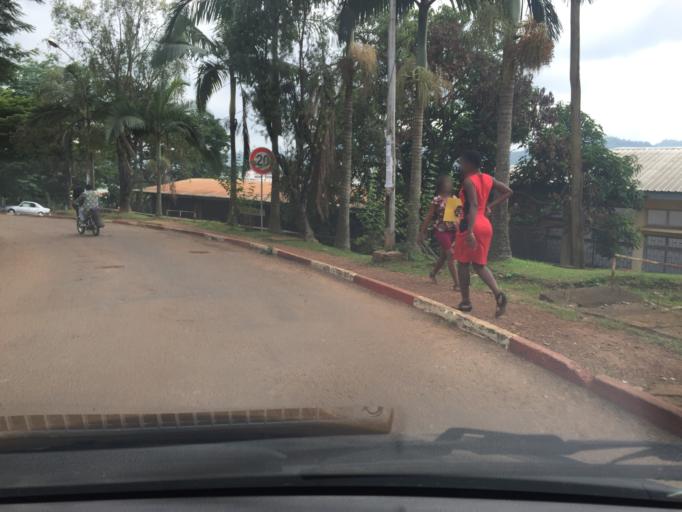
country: CM
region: Centre
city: Yaounde
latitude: 3.8590
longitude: 11.5017
